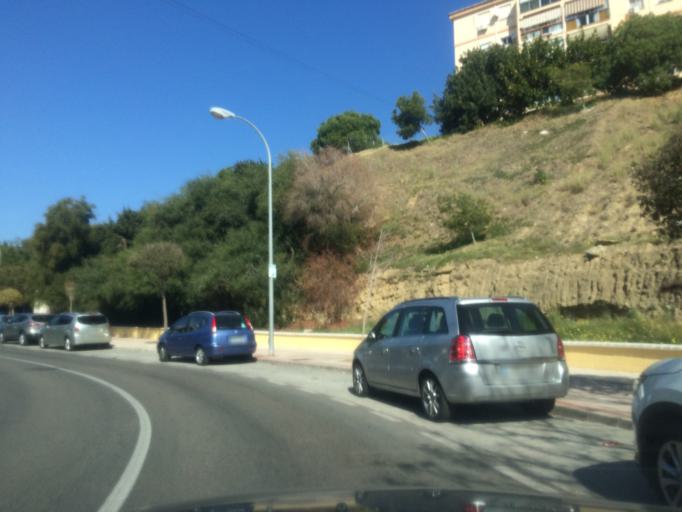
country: ES
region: Andalusia
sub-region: Provincia de Malaga
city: Malaga
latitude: 36.7445
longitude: -4.4183
